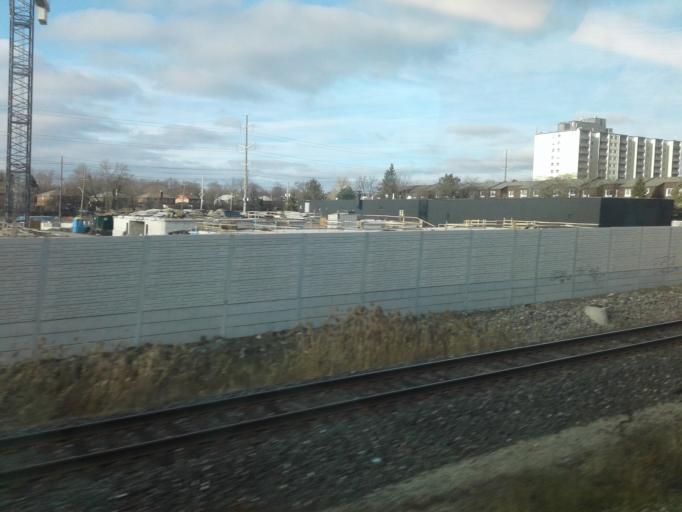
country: CA
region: Ontario
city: Mississauga
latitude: 43.5097
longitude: -79.6376
